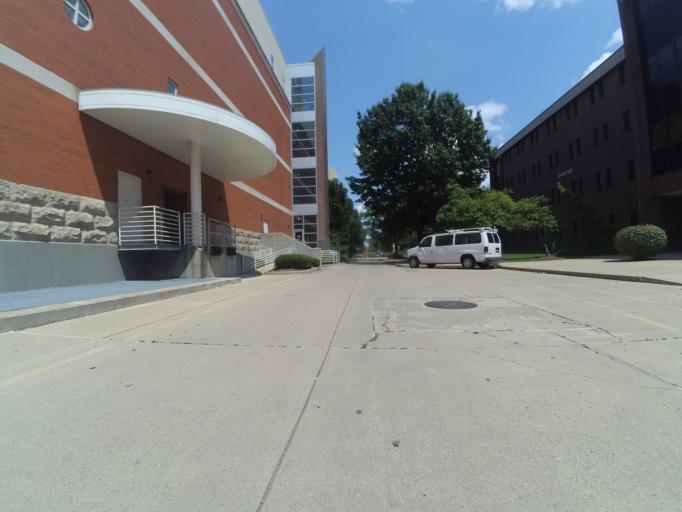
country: US
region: West Virginia
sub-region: Cabell County
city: Huntington
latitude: 38.4223
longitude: -82.4310
